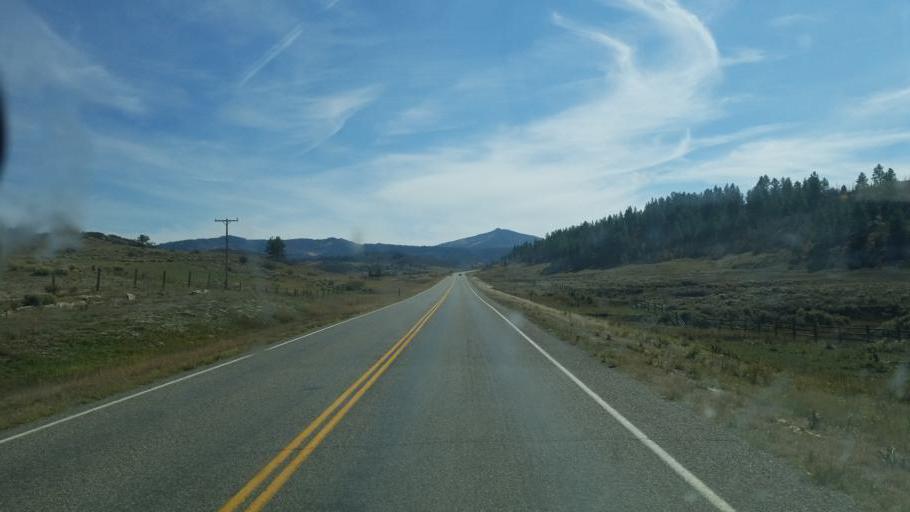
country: US
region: New Mexico
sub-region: Rio Arriba County
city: Dulce
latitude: 37.0200
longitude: -106.8148
